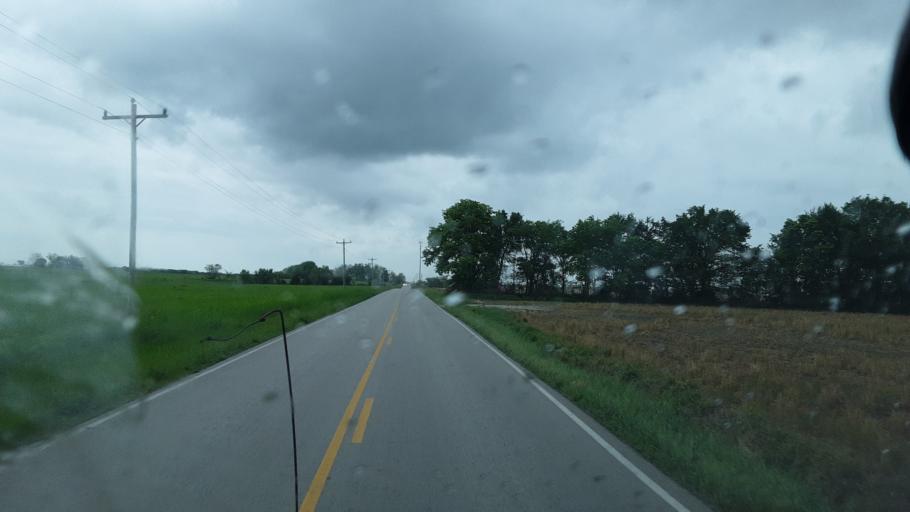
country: US
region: Missouri
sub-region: Boone County
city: Centralia
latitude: 39.4143
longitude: -92.2099
